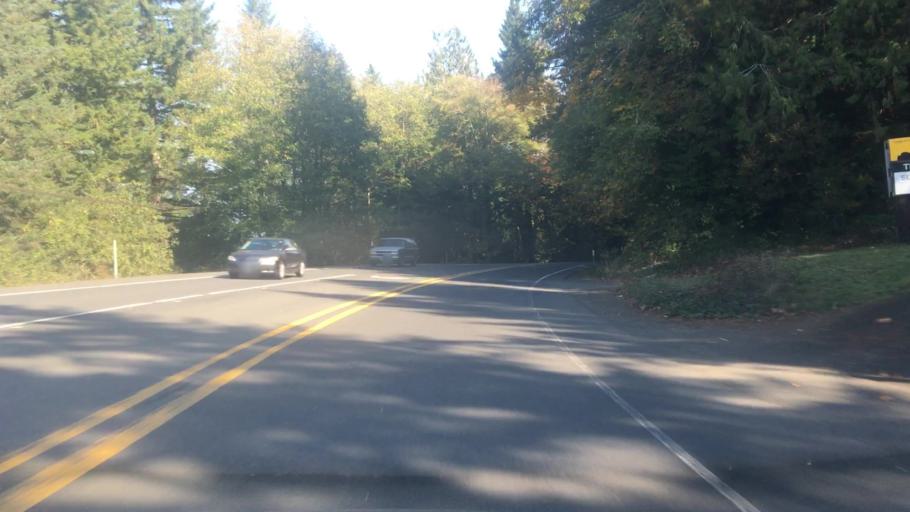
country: US
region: Oregon
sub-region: Lincoln County
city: Rose Lodge
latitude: 45.0117
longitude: -123.8788
